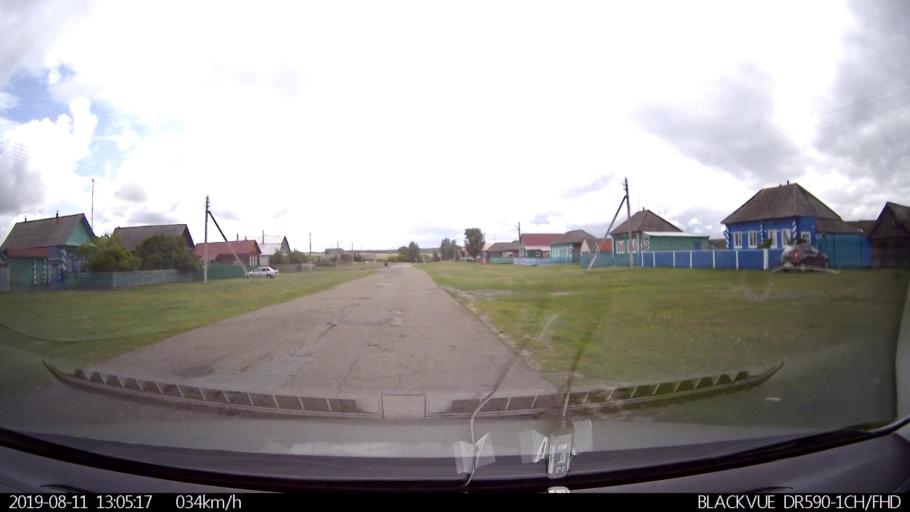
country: RU
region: Ulyanovsk
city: Ignatovka
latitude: 53.8715
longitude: 47.6494
